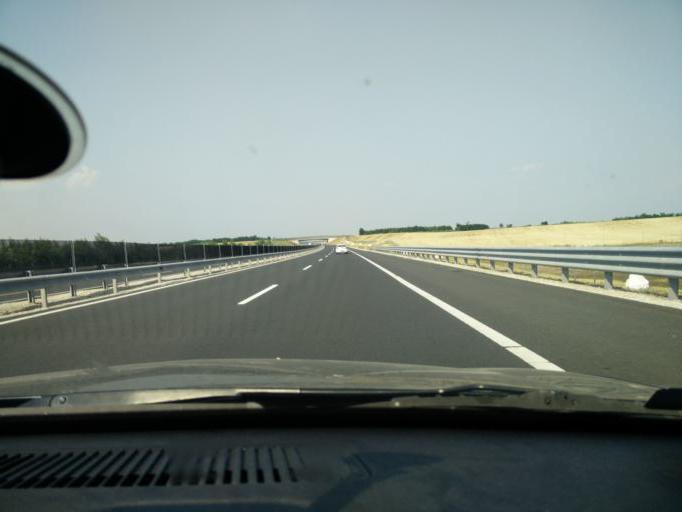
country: HU
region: Tolna
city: Tengelic
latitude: 46.4854
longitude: 18.7479
